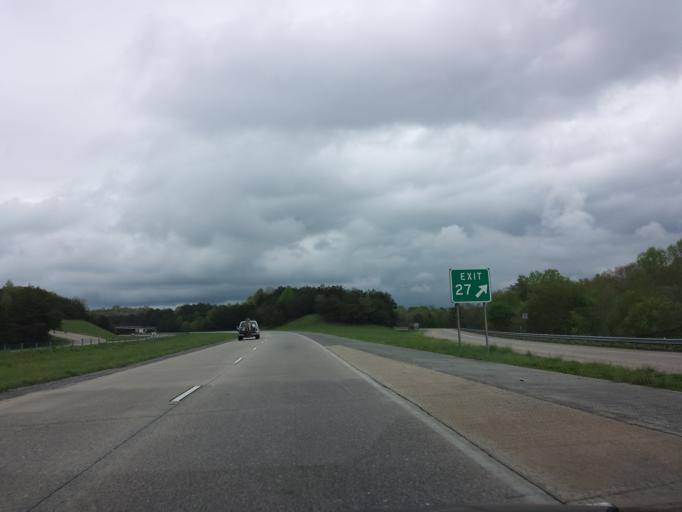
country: US
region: Georgia
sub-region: Cherokee County
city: Ball Ground
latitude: 34.3231
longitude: -84.3976
